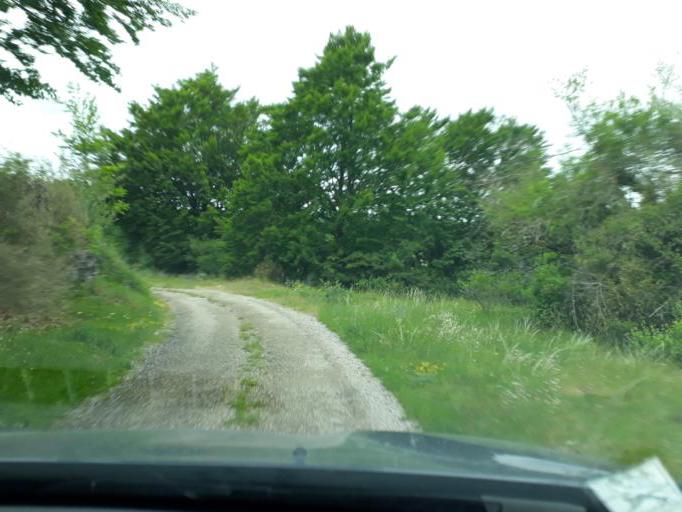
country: FR
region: Languedoc-Roussillon
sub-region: Departement de l'Herault
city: Lodeve
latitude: 43.8118
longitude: 3.2664
